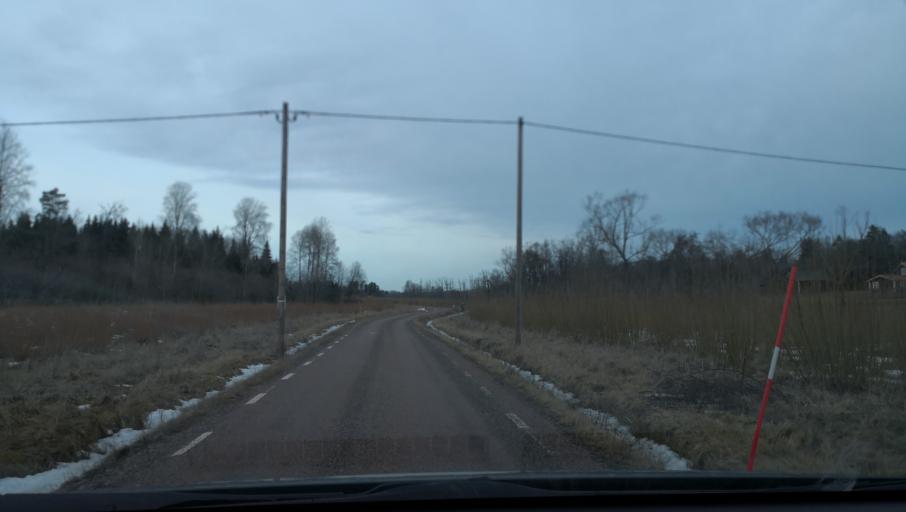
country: SE
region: Vaestmanland
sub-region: Vasteras
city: Skultuna
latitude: 59.6091
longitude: 16.4114
